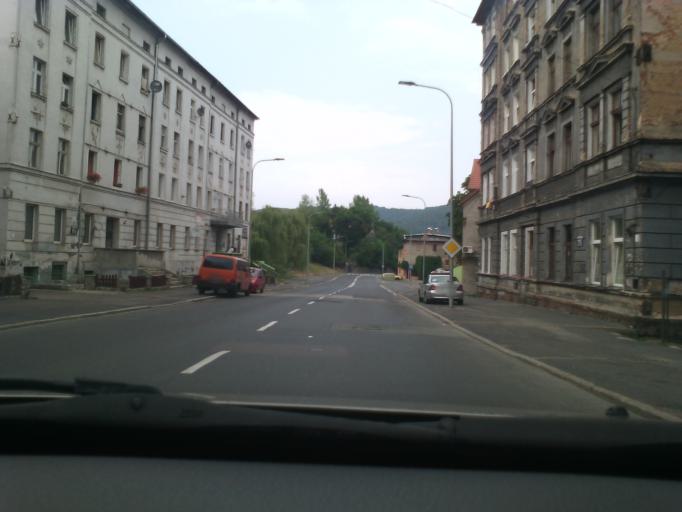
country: PL
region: Lower Silesian Voivodeship
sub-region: Powiat walbrzyski
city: Walbrzych
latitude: 50.7434
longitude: 16.2888
